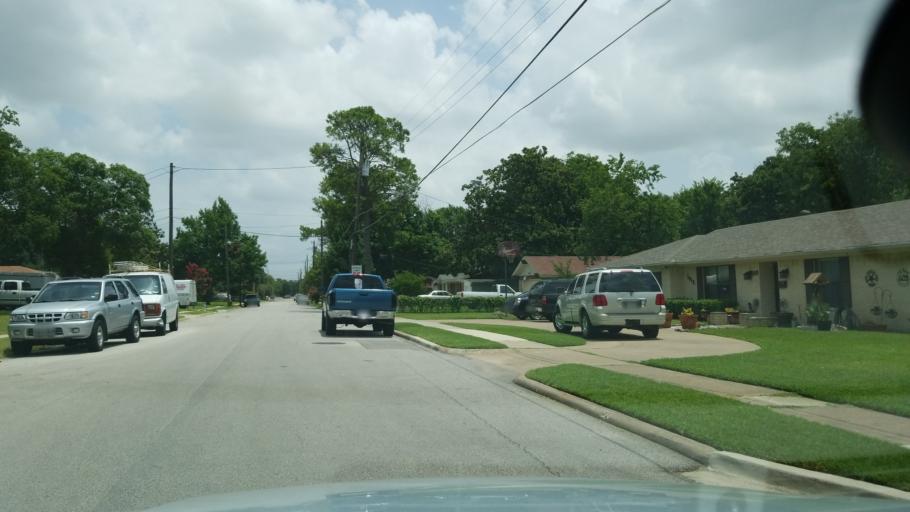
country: US
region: Texas
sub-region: Dallas County
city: Irving
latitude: 32.8277
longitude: -96.9225
